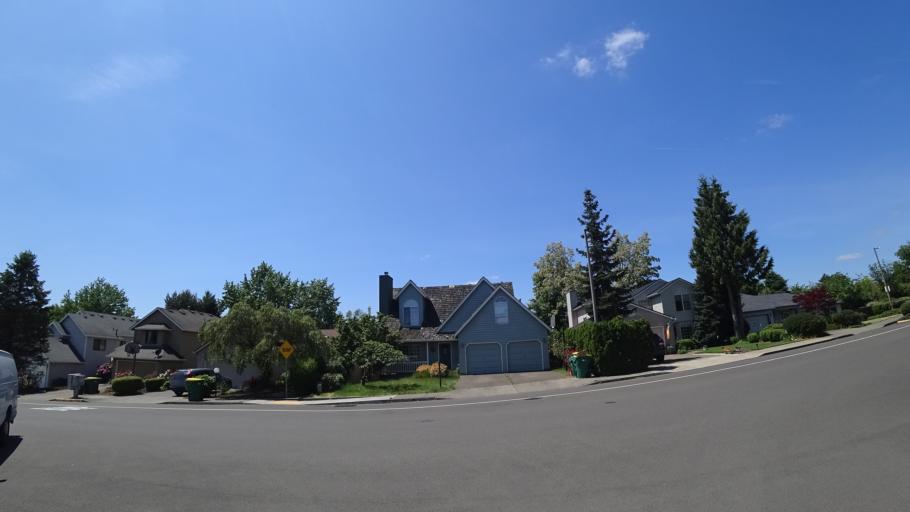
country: US
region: Oregon
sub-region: Washington County
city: Tigard
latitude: 45.4401
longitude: -122.8048
